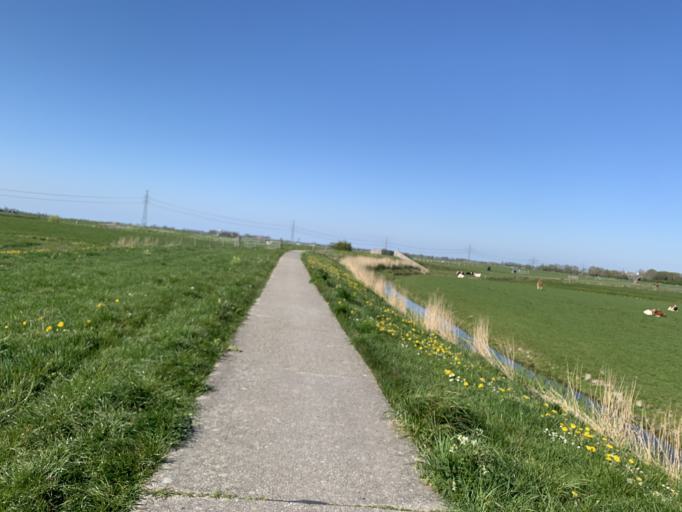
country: NL
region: Groningen
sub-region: Gemeente Winsum
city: Winsum
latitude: 53.2822
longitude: 6.5052
